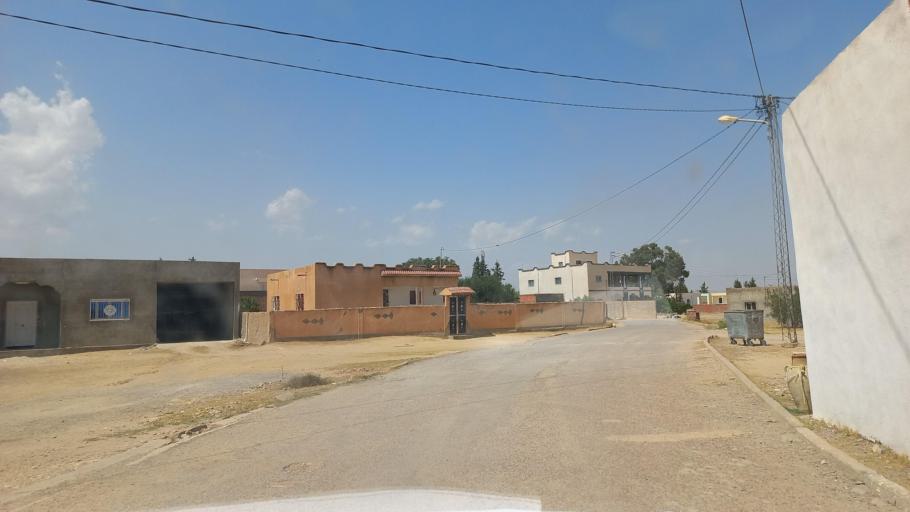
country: TN
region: Al Qasrayn
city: Kasserine
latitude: 35.2488
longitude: 9.0277
